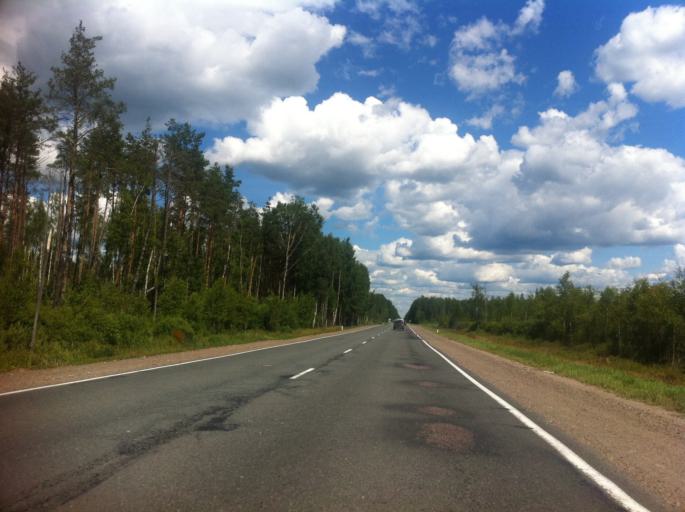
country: RU
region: Pskov
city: Pskov
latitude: 57.8610
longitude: 28.5260
